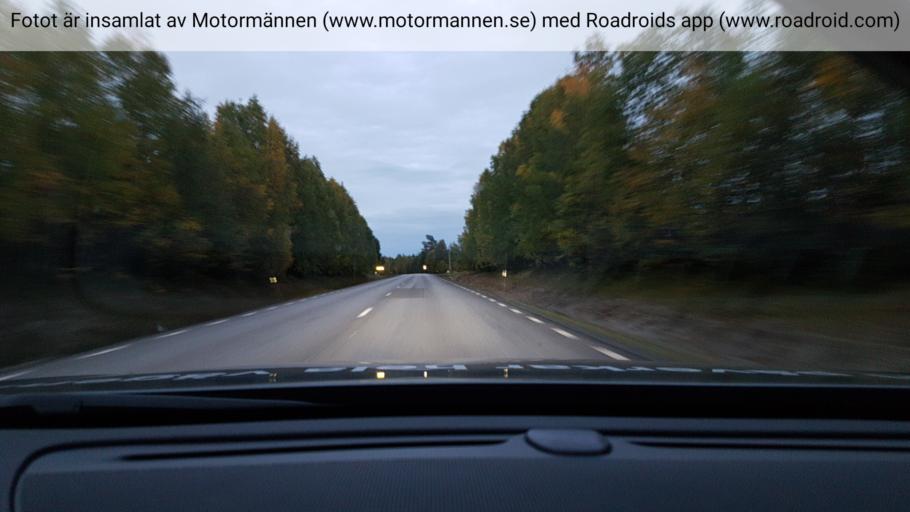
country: SE
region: Norrbotten
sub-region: Alvsbyns Kommun
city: AElvsbyn
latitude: 65.7829
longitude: 20.7614
